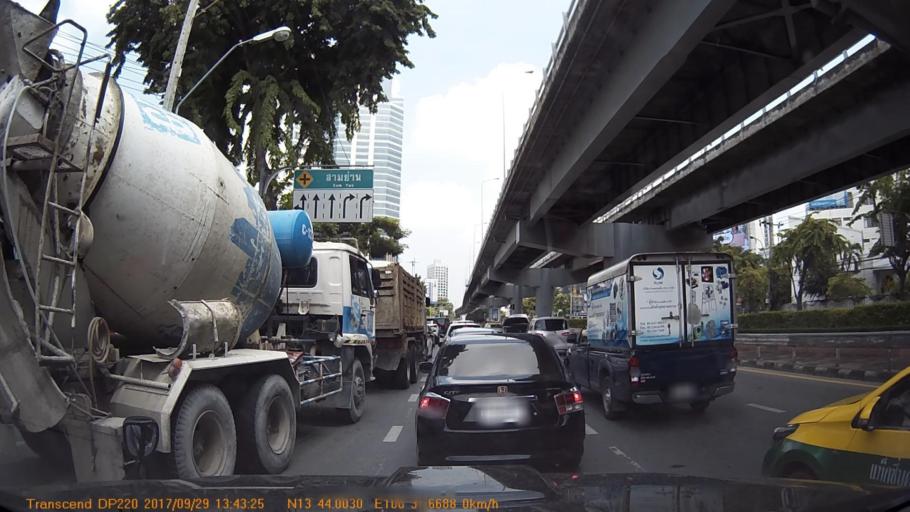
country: TH
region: Bangkok
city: Bang Rak
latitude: 13.7331
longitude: 100.5283
